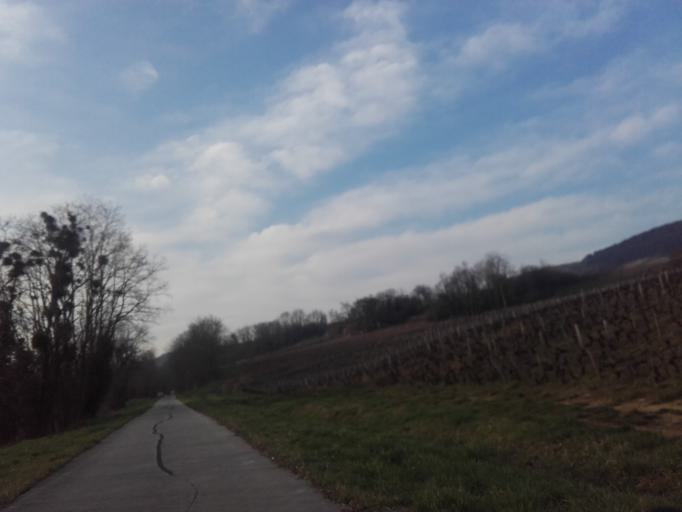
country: FR
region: Bourgogne
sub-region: Departement de la Cote-d'Or
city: Nolay
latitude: 46.9043
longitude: 4.6633
